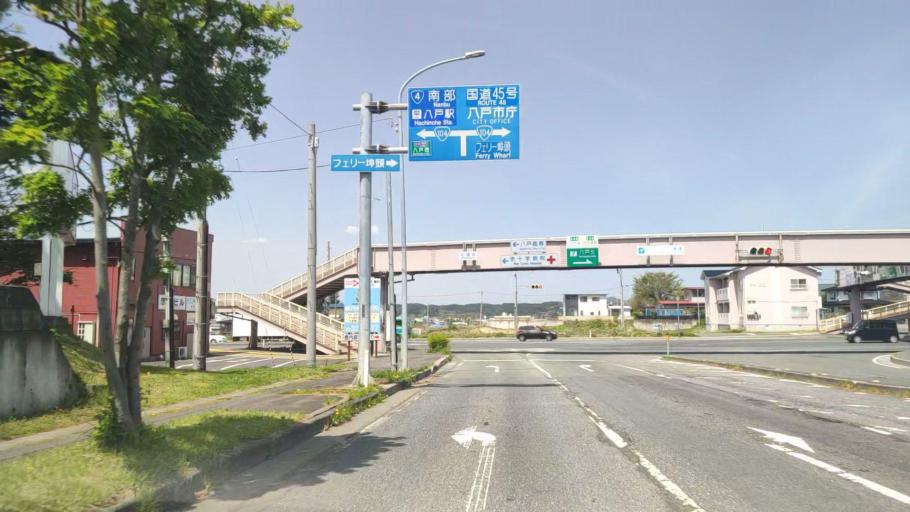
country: JP
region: Aomori
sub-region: Hachinohe Shi
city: Uchimaru
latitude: 40.5015
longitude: 141.4548
